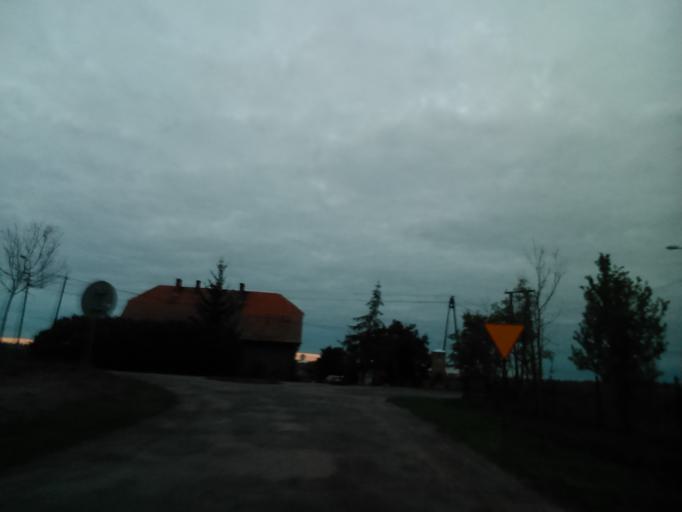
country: PL
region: Kujawsko-Pomorskie
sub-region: Powiat golubsko-dobrzynski
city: Kowalewo Pomorskie
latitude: 53.1201
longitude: 18.8952
